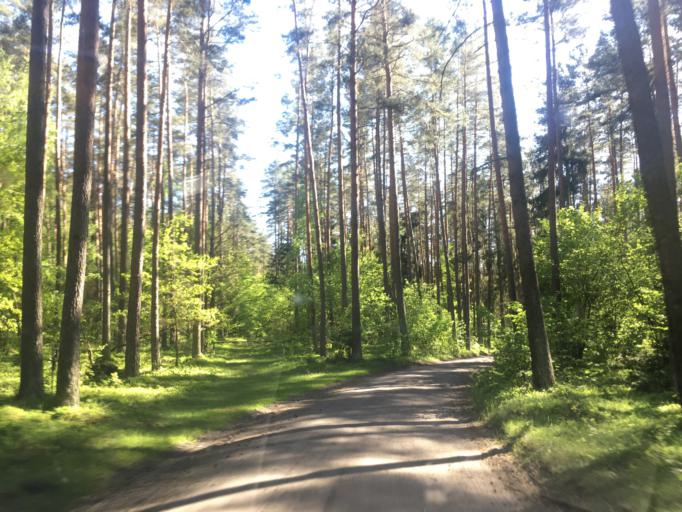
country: PL
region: Warmian-Masurian Voivodeship
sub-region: Powiat mragowski
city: Mikolajki
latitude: 53.7458
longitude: 21.6123
